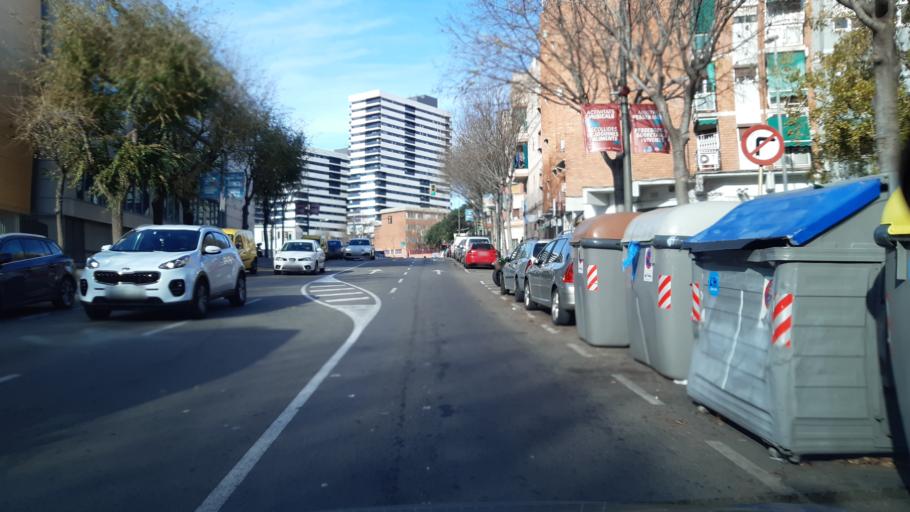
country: ES
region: Catalonia
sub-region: Provincia de Barcelona
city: L'Hospitalet de Llobregat
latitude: 41.3734
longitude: 2.1125
